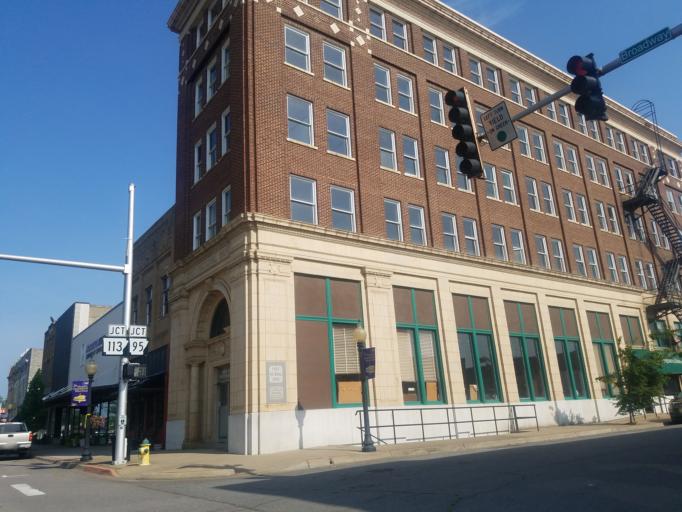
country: US
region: Arkansas
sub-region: Conway County
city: Morrilton
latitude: 35.1524
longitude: -92.7418
